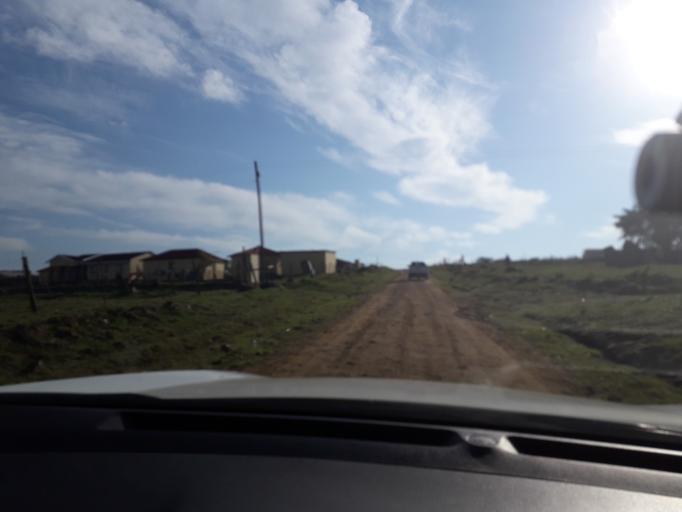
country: ZA
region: Eastern Cape
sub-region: Buffalo City Metropolitan Municipality
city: Bhisho
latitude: -32.9401
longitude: 27.2898
